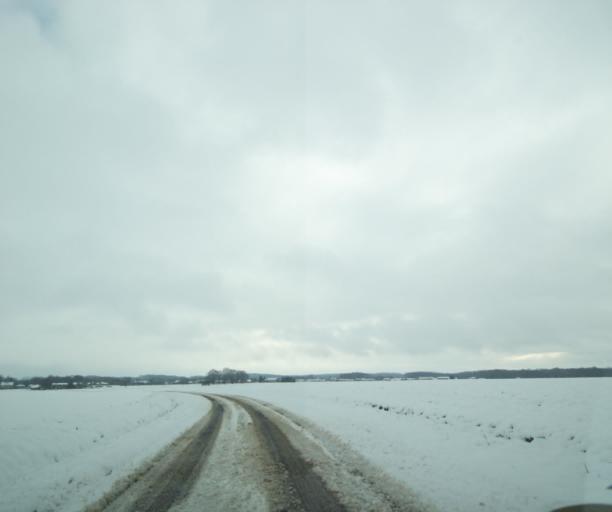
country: FR
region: Champagne-Ardenne
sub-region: Departement de la Haute-Marne
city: Montier-en-Der
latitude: 48.4979
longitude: 4.6887
